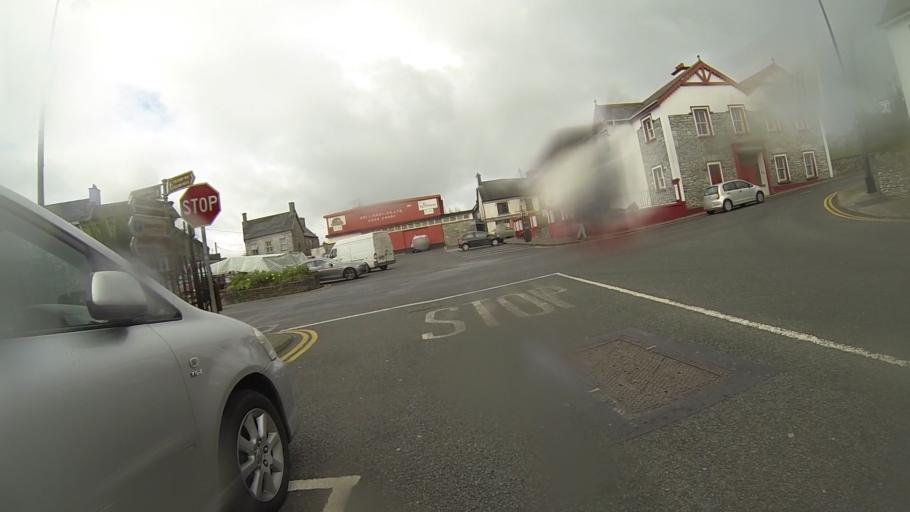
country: IE
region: Munster
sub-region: Ciarrai
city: Kenmare
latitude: 51.8808
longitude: -9.5840
